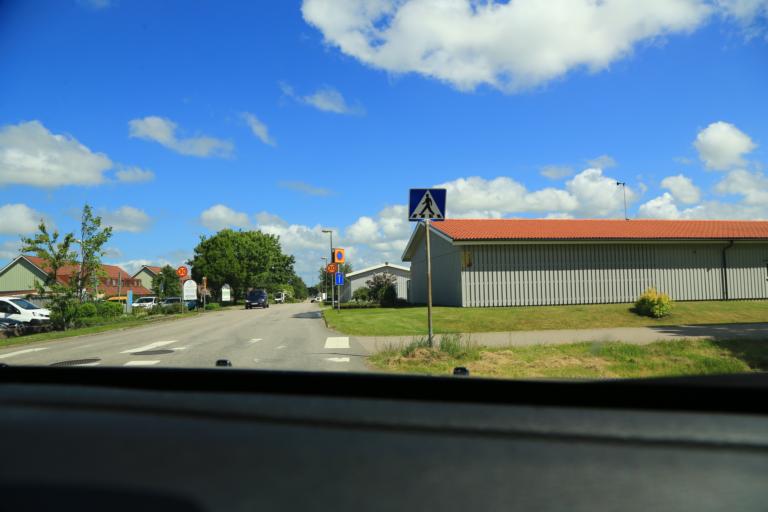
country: SE
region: Halland
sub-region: Varbergs Kommun
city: Varberg
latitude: 57.1114
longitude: 12.2839
